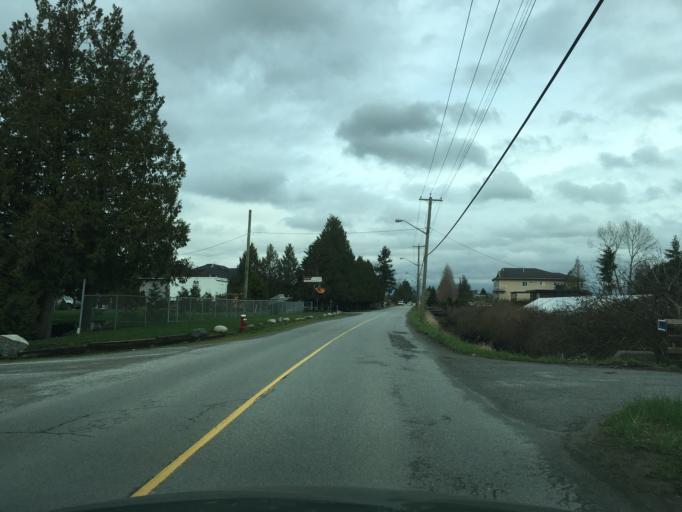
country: CA
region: British Columbia
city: Ladner
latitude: 49.1405
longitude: -123.0694
